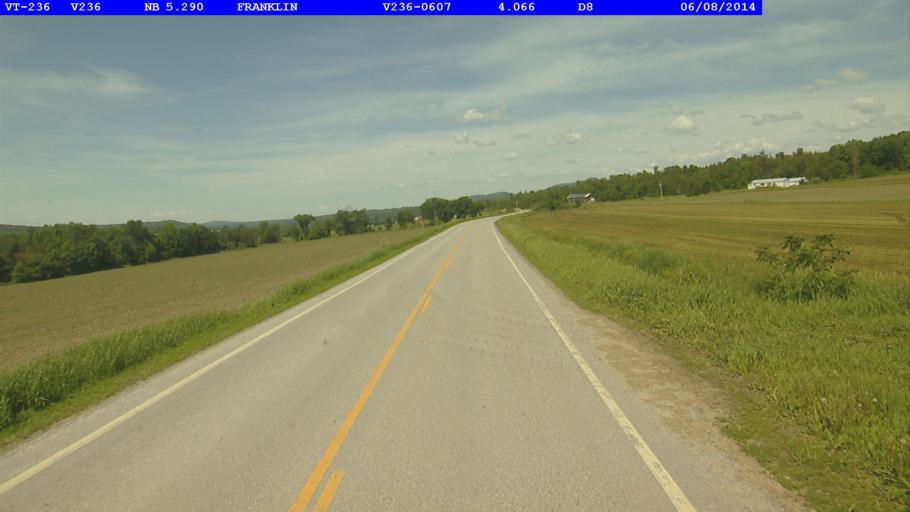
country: US
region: Vermont
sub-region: Franklin County
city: Enosburg Falls
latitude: 44.9830
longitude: -72.8410
